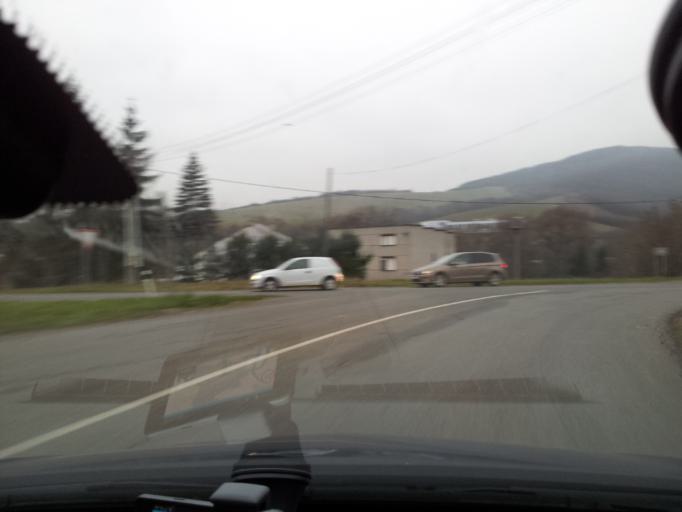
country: SK
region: Presovsky
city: Giraltovce
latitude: 49.0316
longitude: 21.5162
